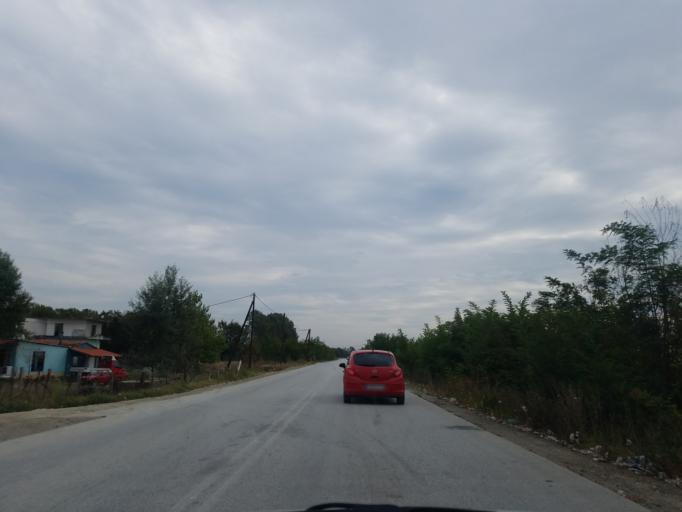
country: GR
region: Thessaly
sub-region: Nomos Kardhitsas
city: Sofades
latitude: 39.3248
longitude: 22.1005
